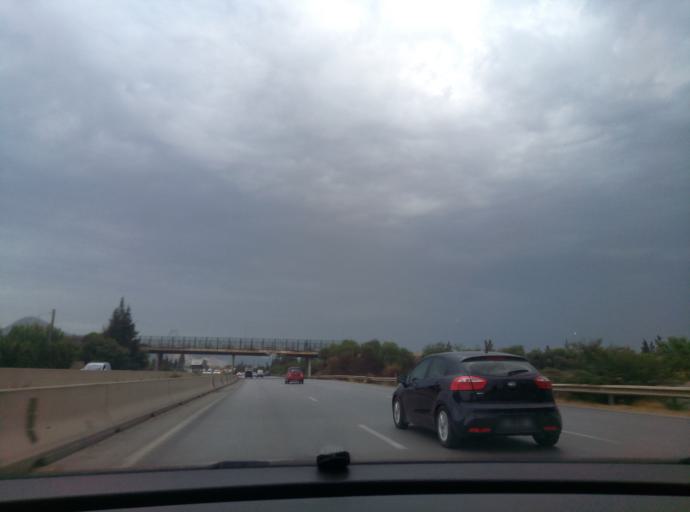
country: TN
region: Tunis
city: La Sebala du Mornag
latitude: 36.7179
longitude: 10.2677
